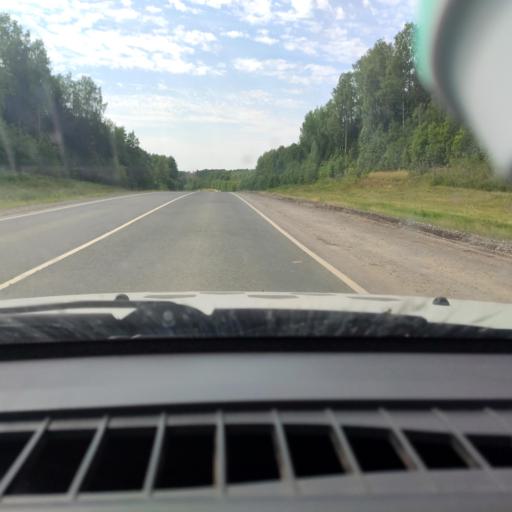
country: RU
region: Kirov
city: Kostino
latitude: 58.8329
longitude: 53.5065
